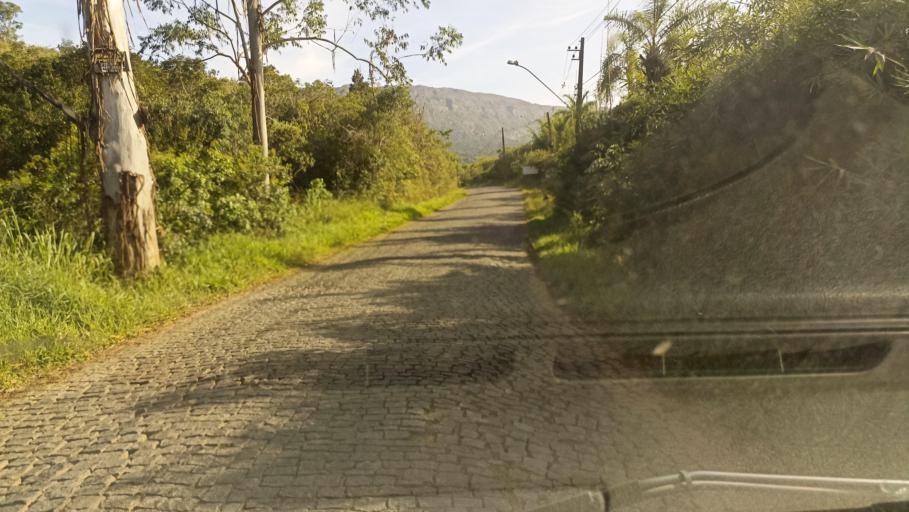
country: BR
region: Minas Gerais
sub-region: Tiradentes
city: Tiradentes
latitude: -21.1188
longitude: -44.1898
